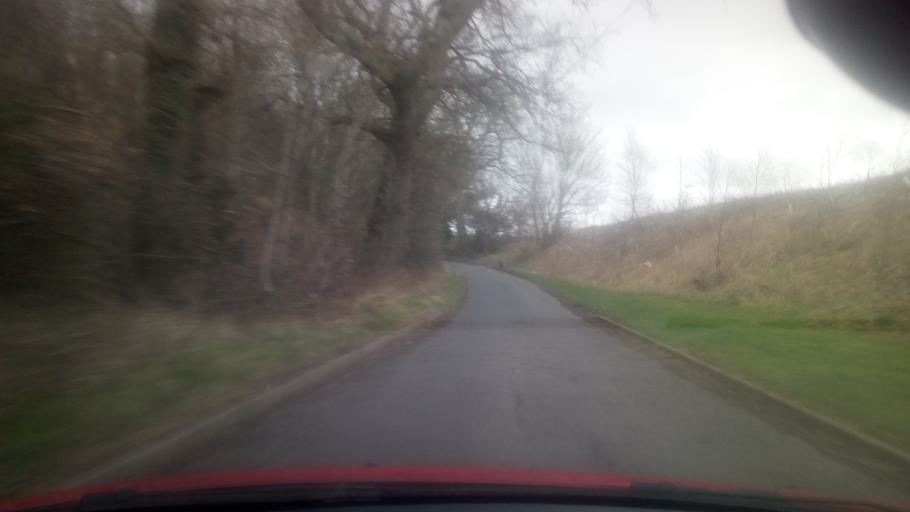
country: GB
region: Scotland
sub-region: The Scottish Borders
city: Jedburgh
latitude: 55.4767
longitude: -2.5438
